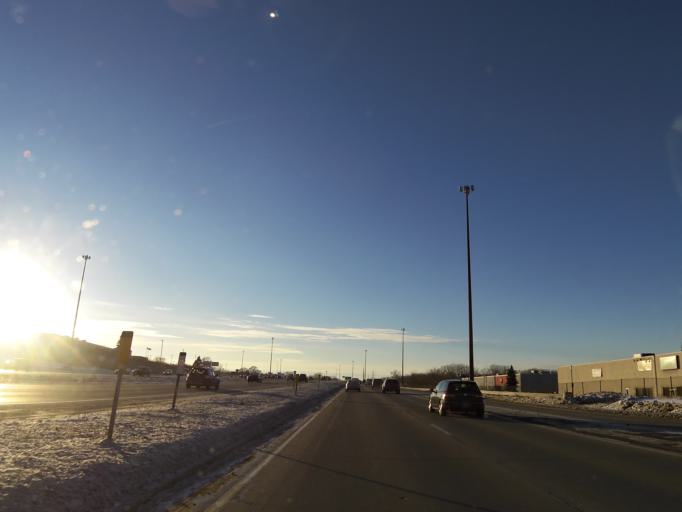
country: US
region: Minnesota
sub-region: Hennepin County
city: Eden Prairie
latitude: 44.8621
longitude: -93.4639
